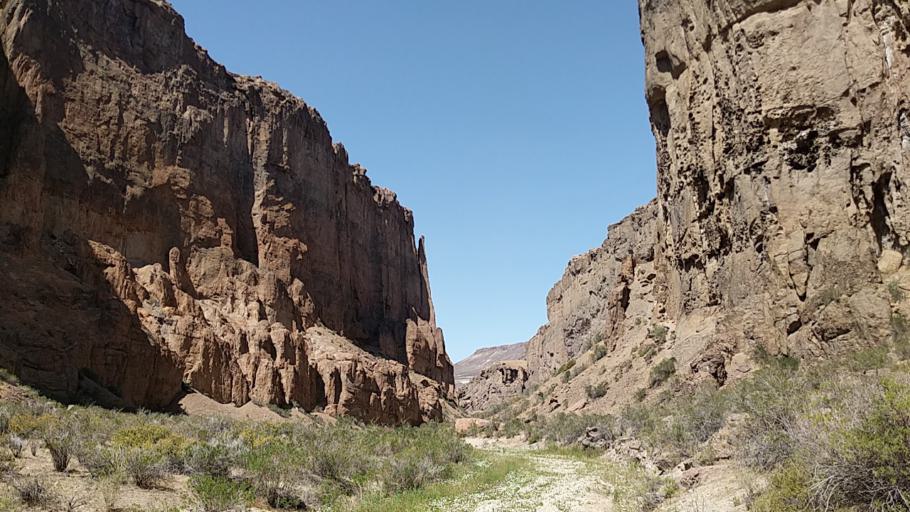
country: AR
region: Chubut
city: Gastre
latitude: -42.6442
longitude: -70.1015
